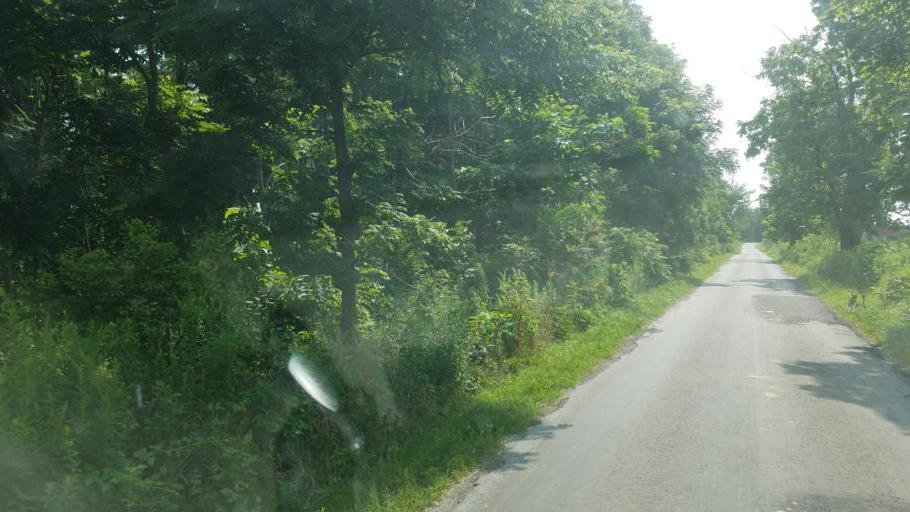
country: US
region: Ohio
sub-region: Hardin County
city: Kenton
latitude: 40.6197
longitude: -83.5254
